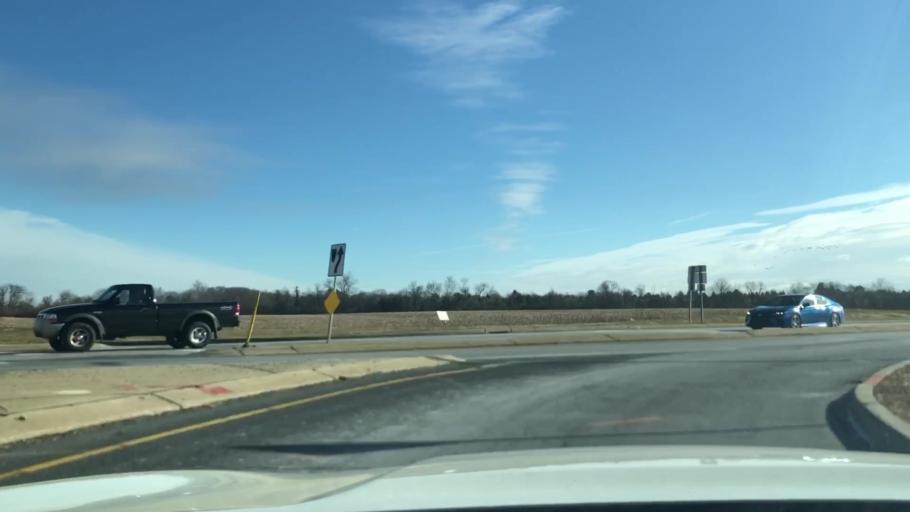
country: US
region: Pennsylvania
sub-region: Lehigh County
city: Catasauqua
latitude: 40.6656
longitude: -75.4198
